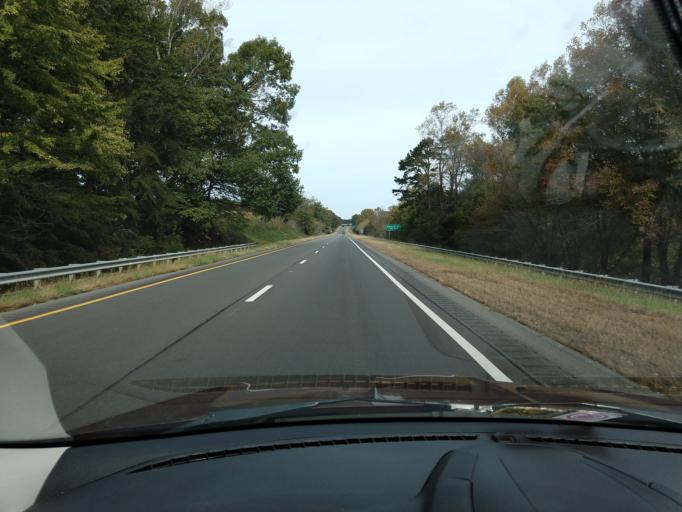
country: US
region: Virginia
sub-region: Pittsylvania County
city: Gretna
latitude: 36.9432
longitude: -79.3772
